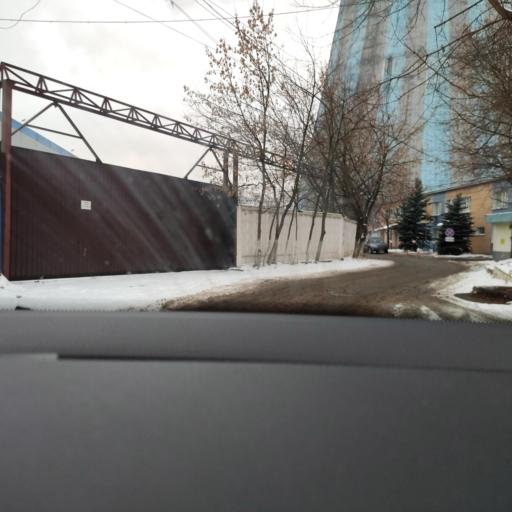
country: RU
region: Moscow
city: Metrogorodok
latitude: 55.8240
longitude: 37.7797
